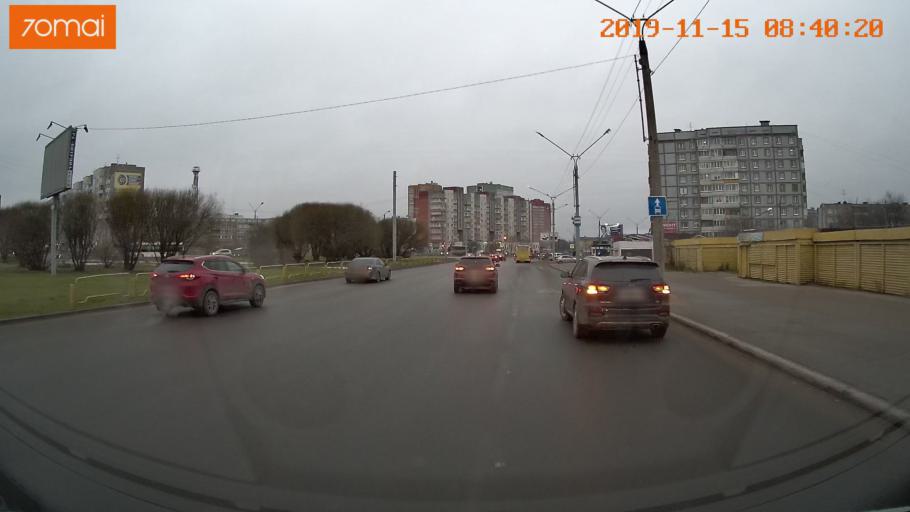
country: RU
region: Vologda
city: Cherepovets
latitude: 59.0943
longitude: 37.9153
